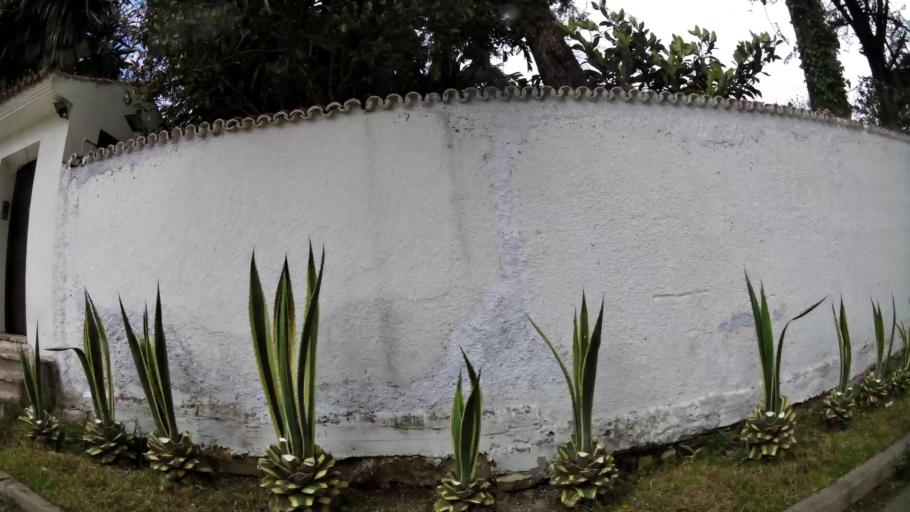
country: MA
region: Tanger-Tetouan
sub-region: Tanger-Assilah
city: Tangier
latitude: 35.7855
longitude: -5.8488
